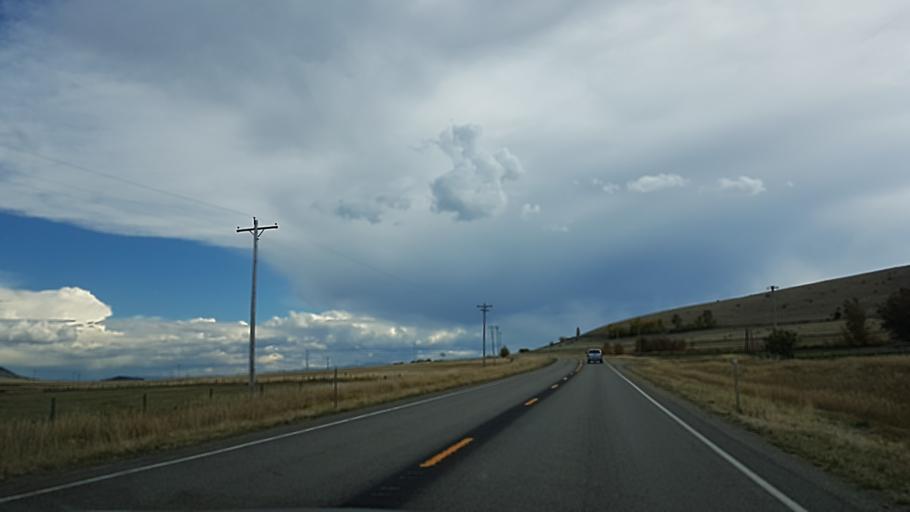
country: US
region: Montana
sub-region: Jefferson County
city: Whitehall
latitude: 45.7795
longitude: -111.9124
